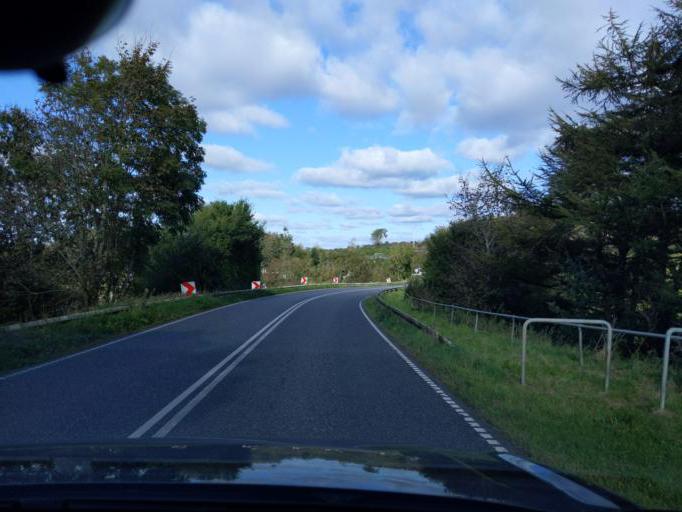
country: DK
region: Central Jutland
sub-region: Viborg Kommune
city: Bjerringbro
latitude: 56.5005
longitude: 9.5842
